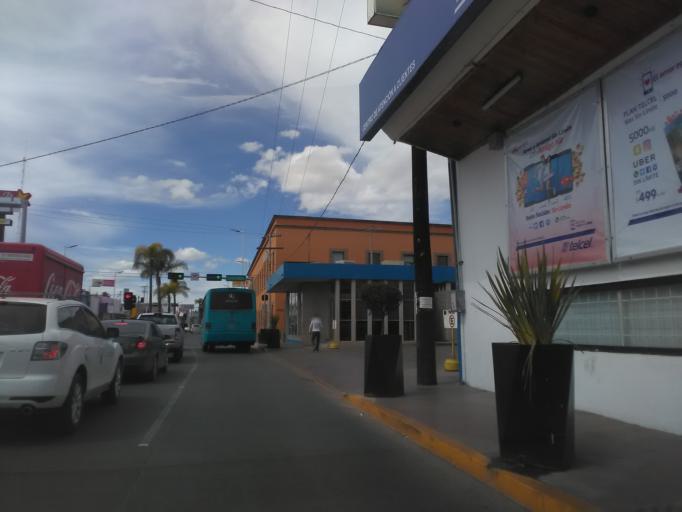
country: MX
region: Durango
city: Victoria de Durango
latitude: 24.0283
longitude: -104.6502
